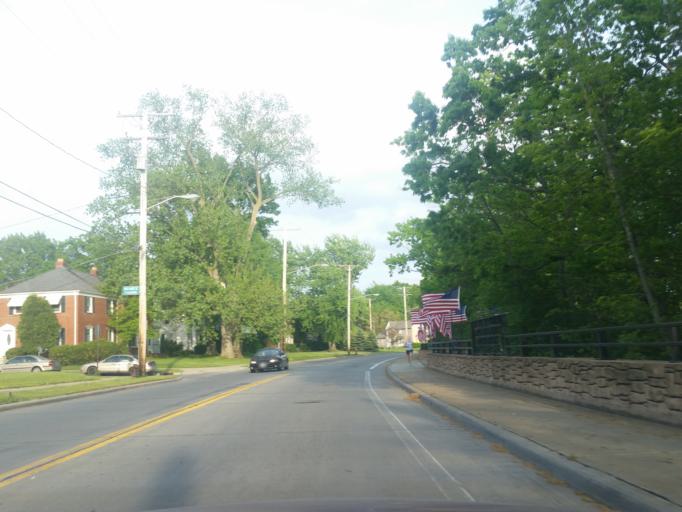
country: US
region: Ohio
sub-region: Cuyahoga County
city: Lakewood
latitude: 41.4677
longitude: -81.8162
